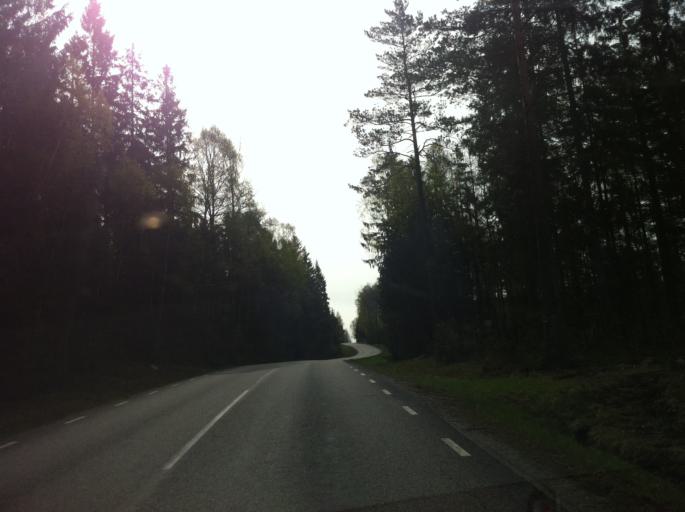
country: SE
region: Vaestra Goetaland
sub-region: Marks Kommun
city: Kinna
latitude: 57.4468
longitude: 12.7342
